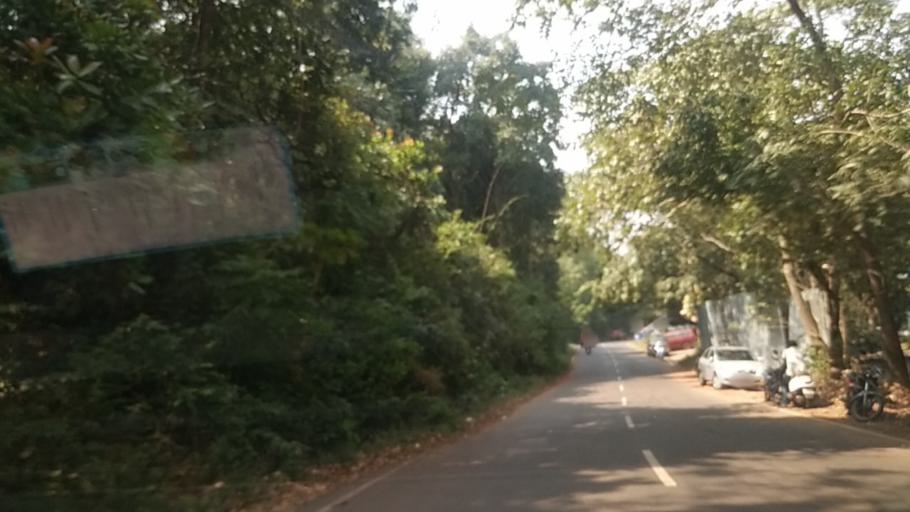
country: IN
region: Goa
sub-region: North Goa
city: Morjim
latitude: 15.6609
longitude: 73.7395
